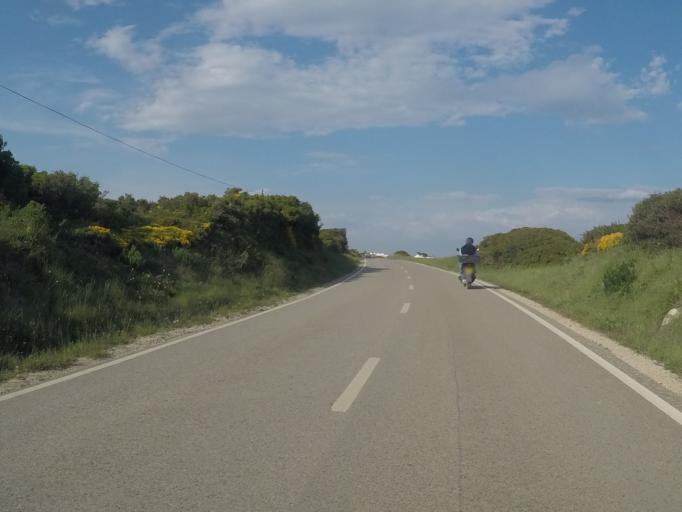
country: PT
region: Setubal
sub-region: Sesimbra
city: Sesimbra
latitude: 38.4218
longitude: -9.1997
